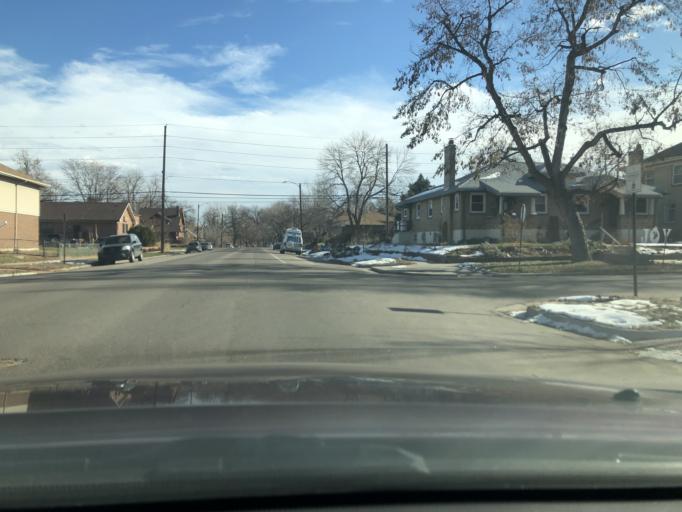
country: US
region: Colorado
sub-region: Denver County
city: Denver
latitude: 39.7494
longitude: -104.9626
